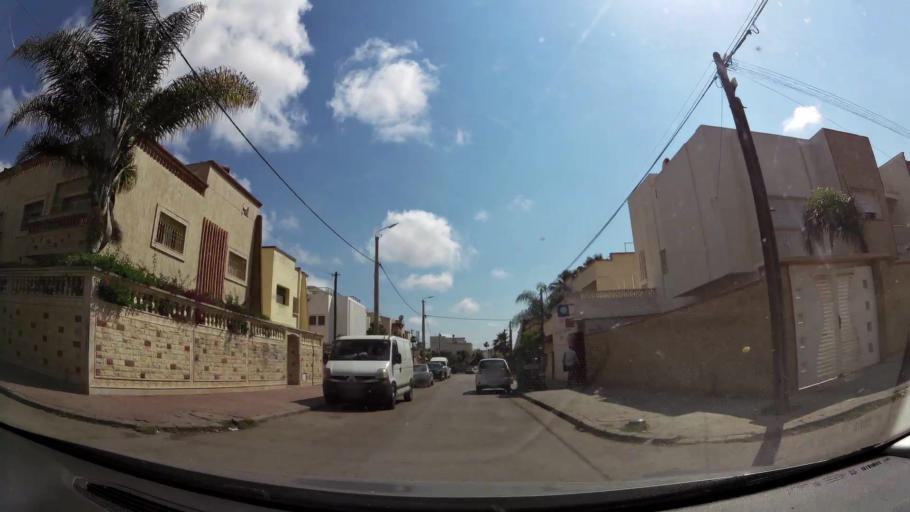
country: MA
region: Rabat-Sale-Zemmour-Zaer
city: Sale
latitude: 34.0366
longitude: -6.7871
